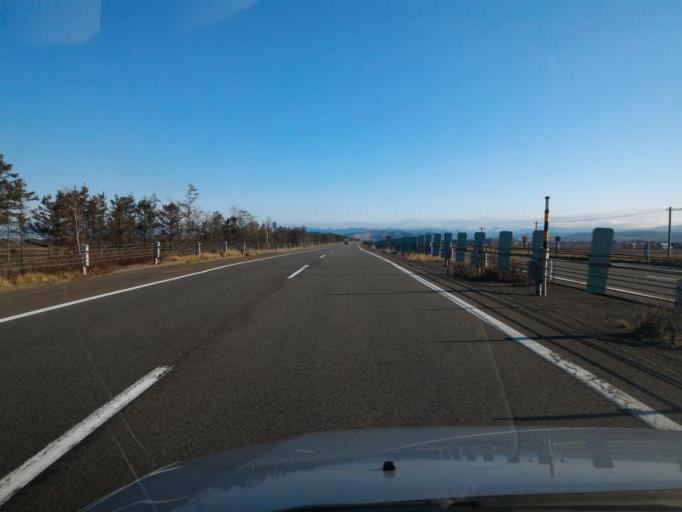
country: JP
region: Hokkaido
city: Iwamizawa
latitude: 43.1506
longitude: 141.7016
